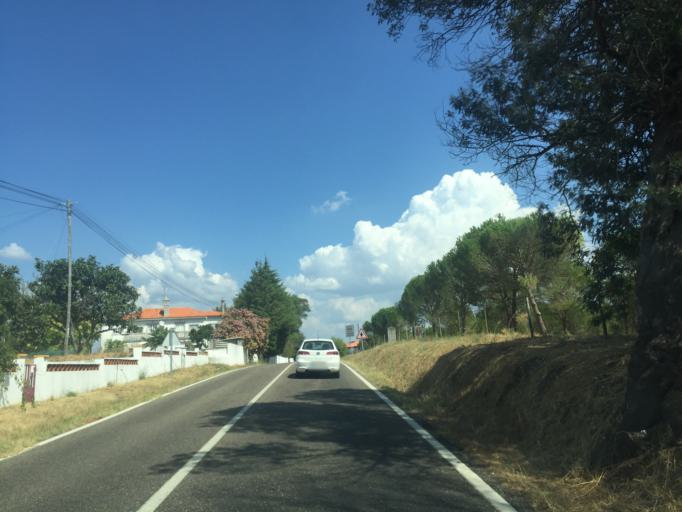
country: PT
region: Santarem
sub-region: Constancia
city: Constancia
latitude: 39.4688
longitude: -8.3822
